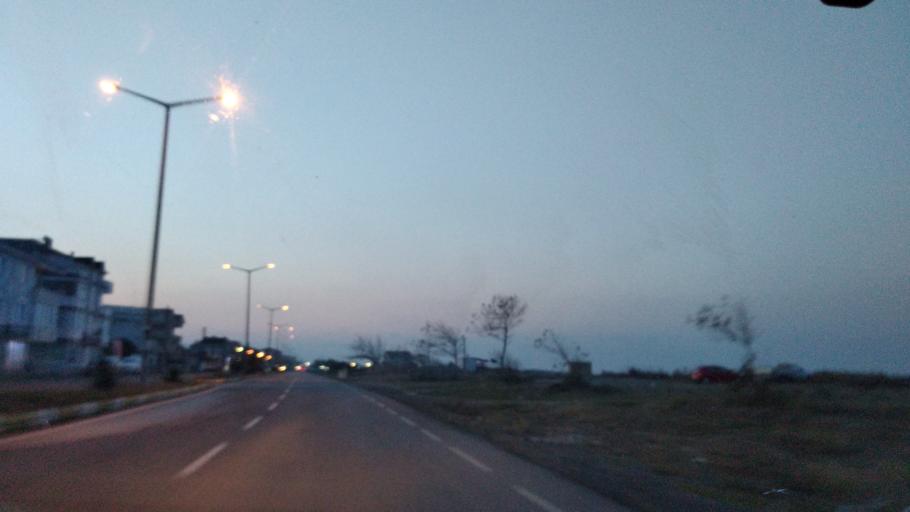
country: TR
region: Sakarya
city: Karasu
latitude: 41.0973
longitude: 30.7277
